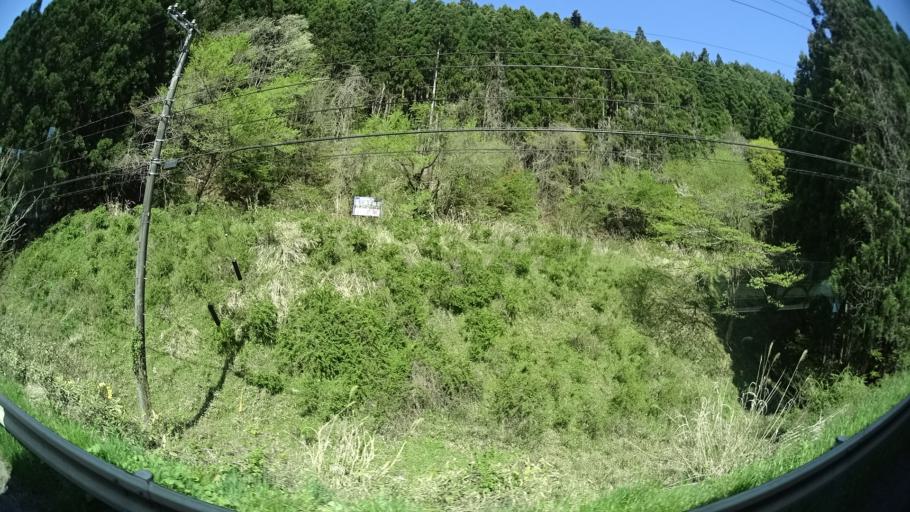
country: JP
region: Iwate
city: Ofunato
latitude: 38.9239
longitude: 141.5931
